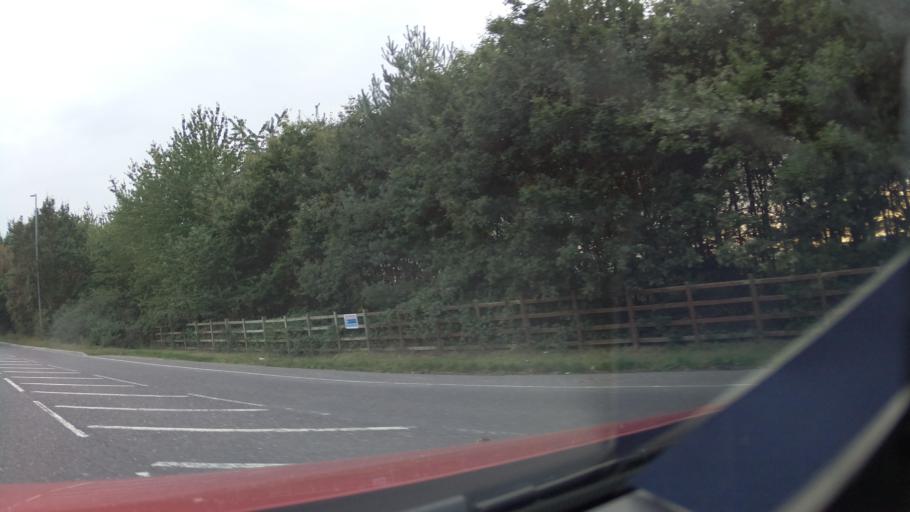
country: GB
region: England
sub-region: Lincolnshire
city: Skellingthorpe
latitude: 53.1531
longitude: -0.6709
